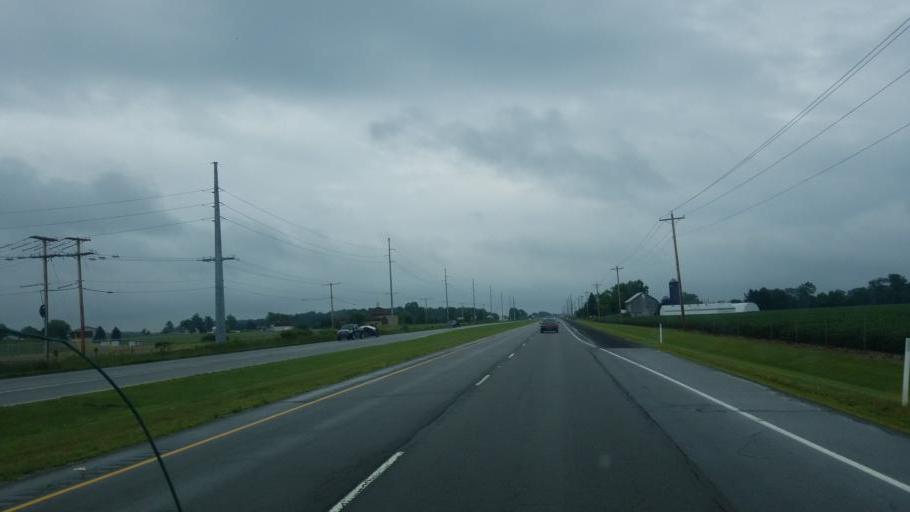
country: US
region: Indiana
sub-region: Wells County
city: Ossian
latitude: 40.9461
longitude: -85.0549
